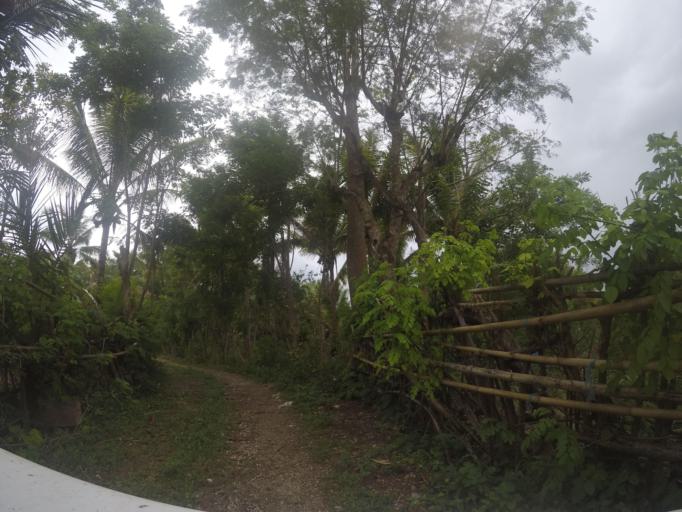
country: TL
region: Lautem
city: Lospalos
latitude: -8.5272
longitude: 126.9923
